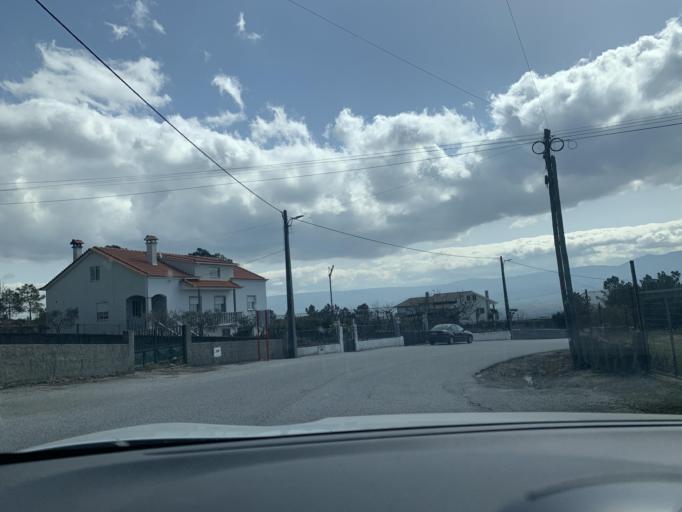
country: PT
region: Guarda
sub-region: Fornos de Algodres
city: Fornos de Algodres
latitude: 40.6129
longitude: -7.6062
